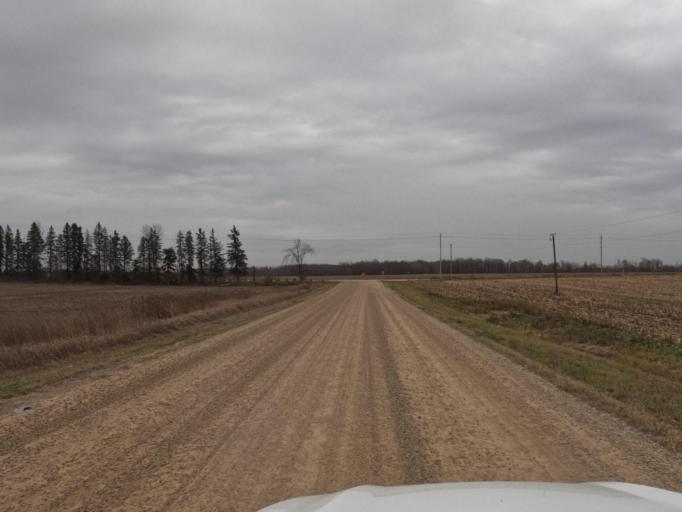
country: CA
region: Ontario
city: Orangeville
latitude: 43.8667
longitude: -80.3548
